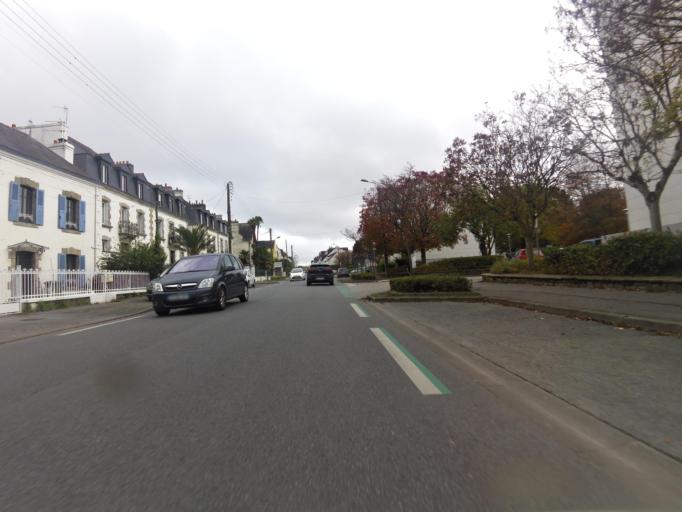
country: FR
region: Brittany
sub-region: Departement du Morbihan
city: Auray
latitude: 47.6734
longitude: -2.9929
